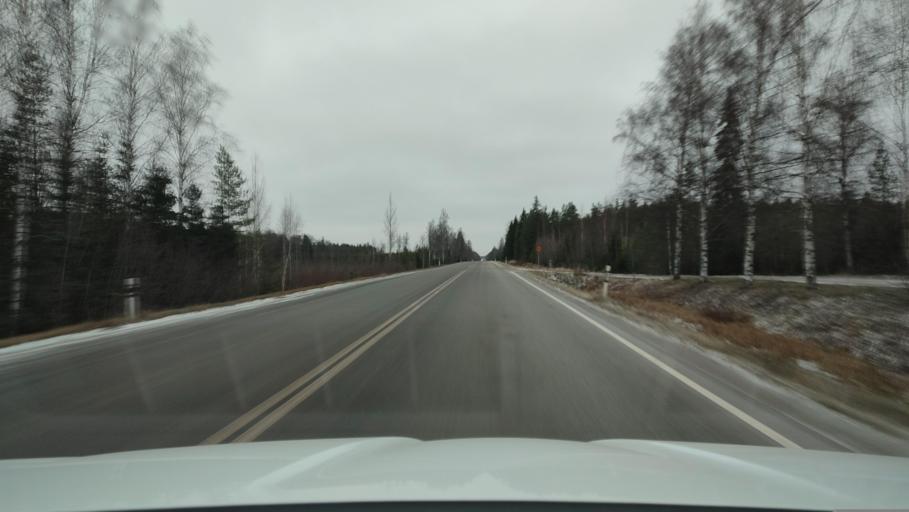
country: FI
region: Ostrobothnia
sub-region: Sydosterbotten
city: Naerpes
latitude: 62.5049
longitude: 21.4505
